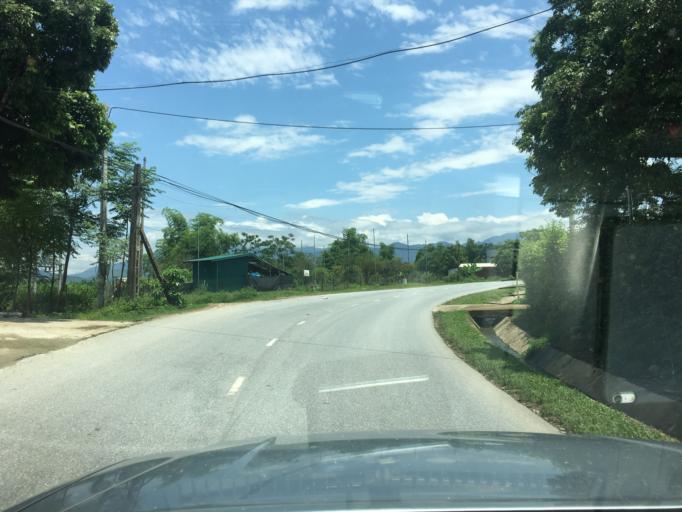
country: VN
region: Yen Bai
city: Son Thinh
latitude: 21.6250
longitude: 104.5091
